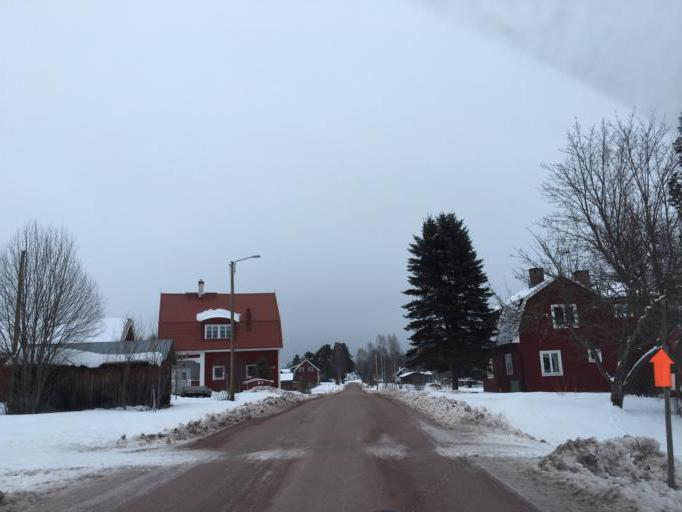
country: SE
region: Dalarna
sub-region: Alvdalens Kommun
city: AElvdalen
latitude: 61.2573
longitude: 14.0540
